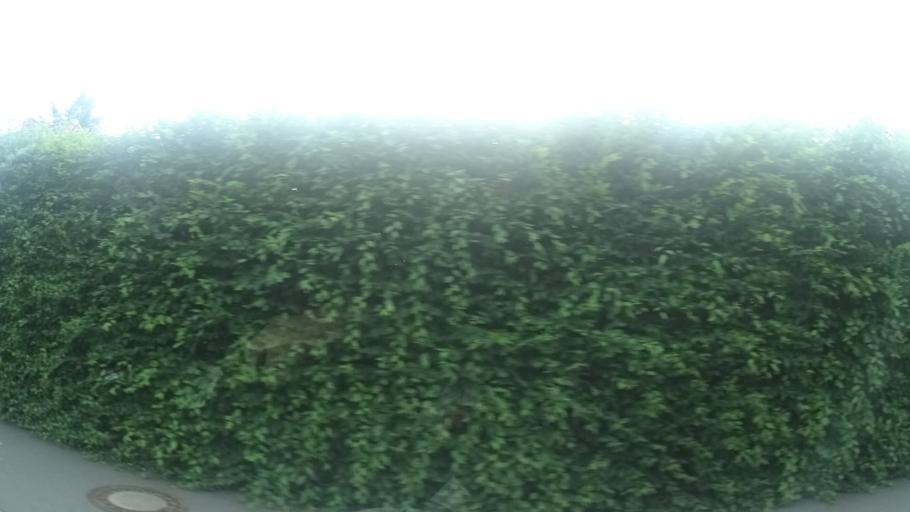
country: DE
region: Lower Saxony
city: Pattensen
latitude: 52.2144
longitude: 9.6999
